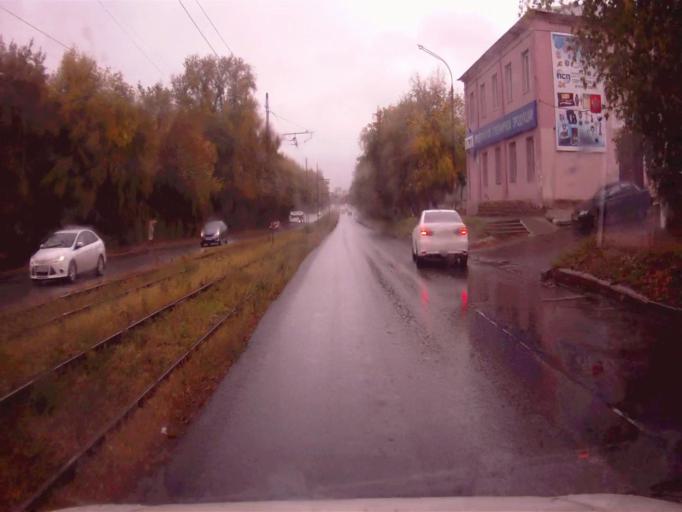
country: RU
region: Chelyabinsk
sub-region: Gorod Chelyabinsk
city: Chelyabinsk
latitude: 55.1784
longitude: 61.4148
